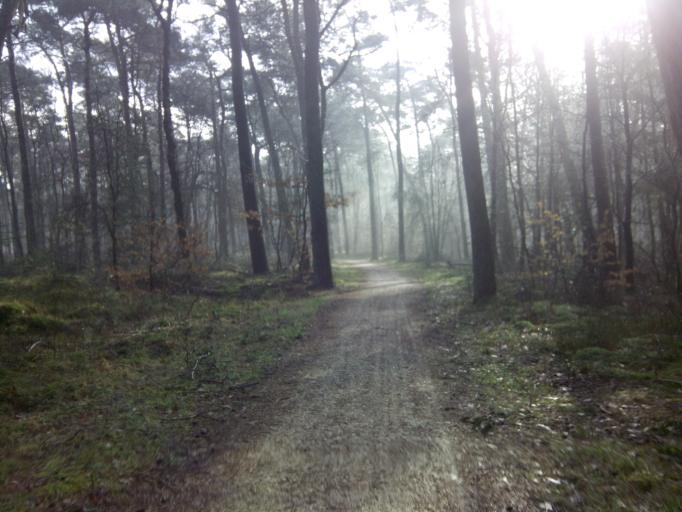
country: NL
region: Utrecht
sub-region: Gemeente Utrechtse Heuvelrug
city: Maarsbergen
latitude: 52.0381
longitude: 5.3881
